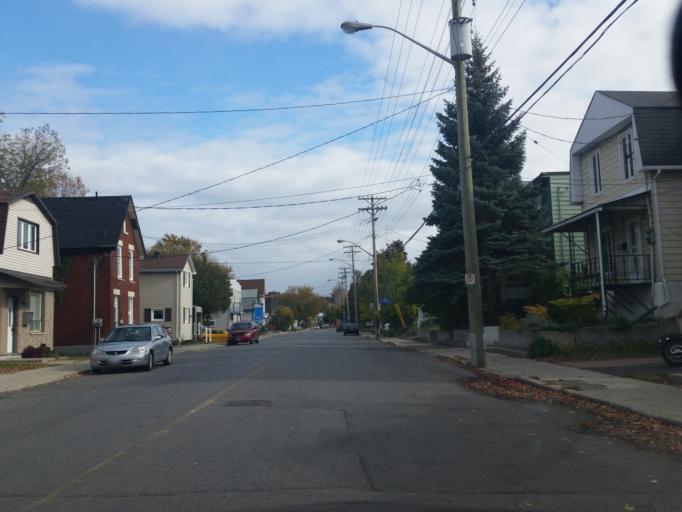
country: CA
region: Ontario
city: Ottawa
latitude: 45.4409
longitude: -75.6684
